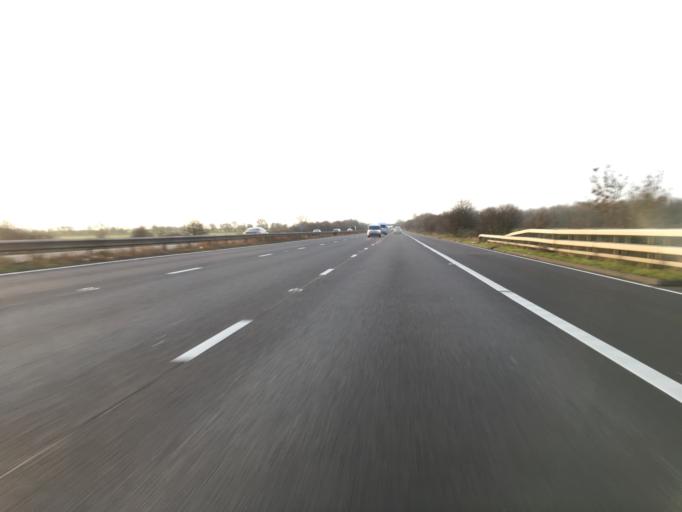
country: GB
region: England
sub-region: Gloucestershire
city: Tewkesbury
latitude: 51.9742
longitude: -2.1275
